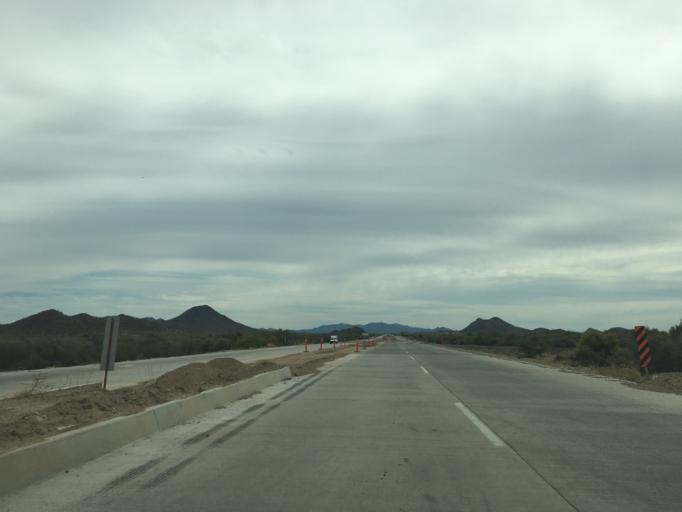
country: MX
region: Sonora
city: Hermosillo
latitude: 28.8682
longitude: -110.9586
